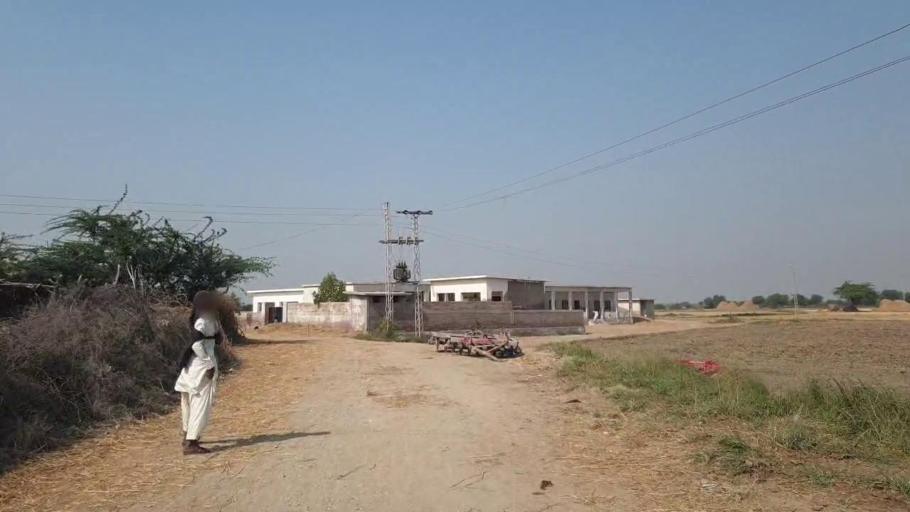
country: PK
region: Sindh
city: Kario
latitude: 24.9389
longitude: 68.5658
